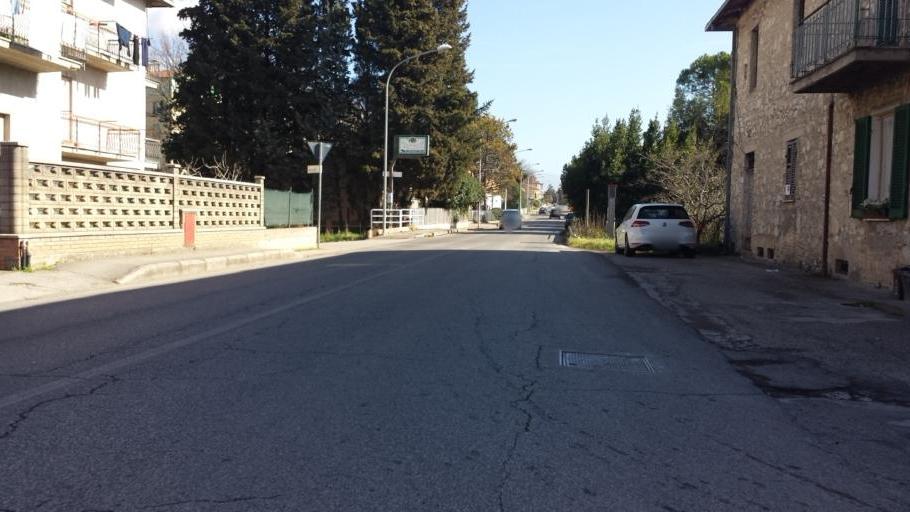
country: IT
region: Umbria
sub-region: Provincia di Terni
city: San Gemini
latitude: 42.5904
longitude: 12.5778
